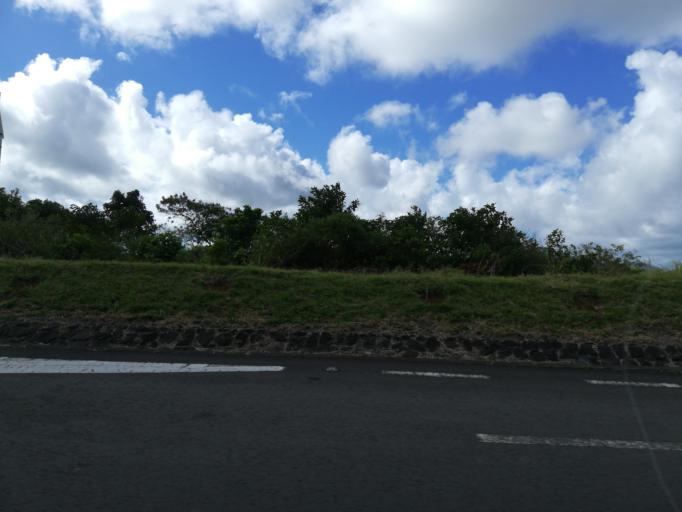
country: MU
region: Grand Port
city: Plaine Magnien
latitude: -20.4228
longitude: 57.6576
